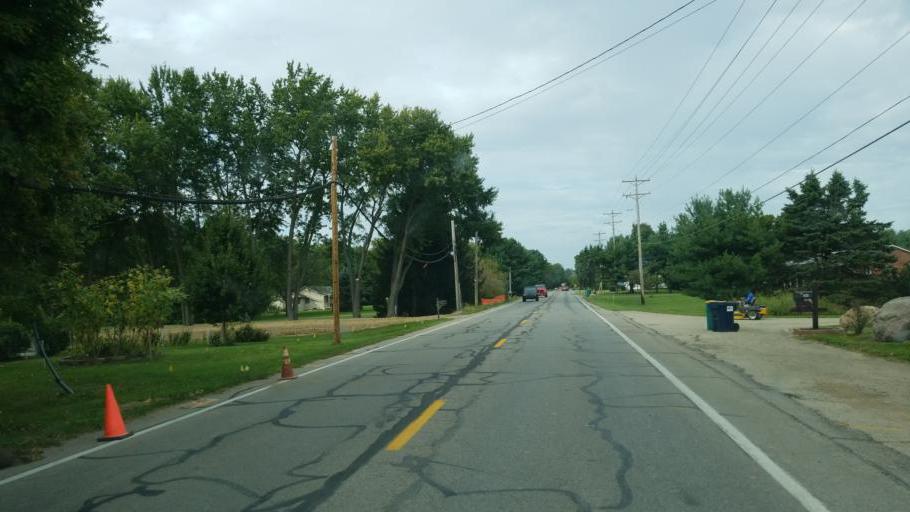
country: US
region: Ohio
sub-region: Franklin County
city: New Albany
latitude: 40.0360
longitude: -82.8117
